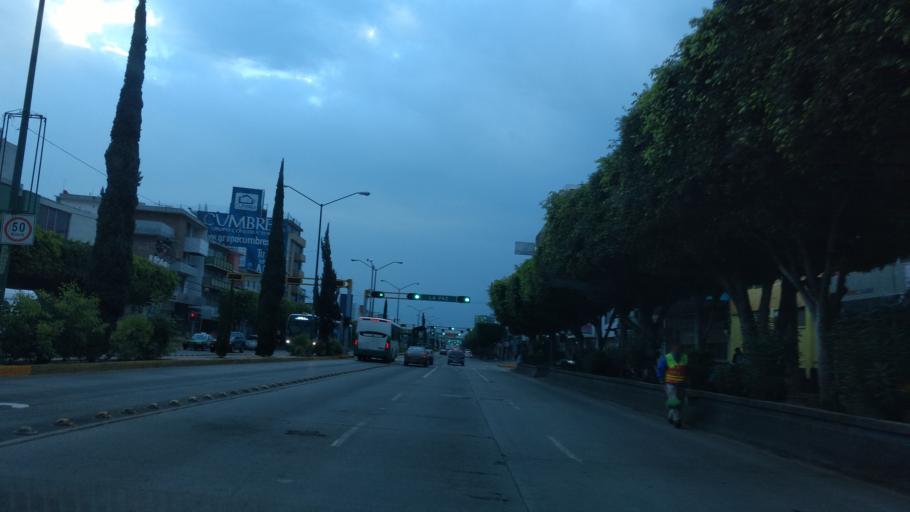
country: MX
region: Guanajuato
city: Leon
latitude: 21.1240
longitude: -101.6785
